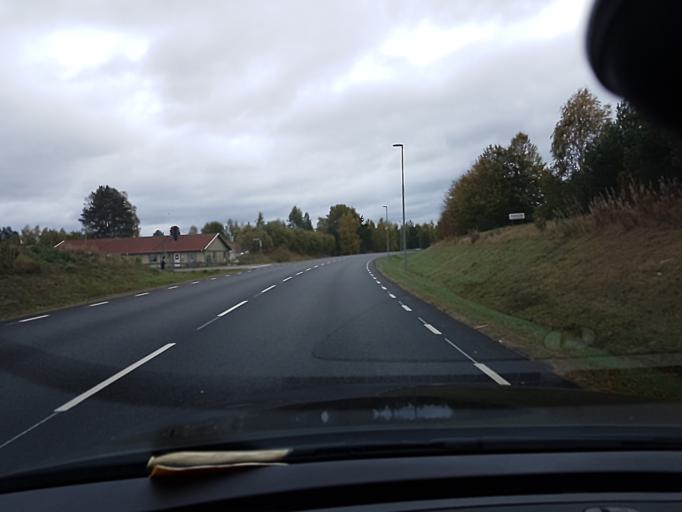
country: SE
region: Kronoberg
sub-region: Vaxjo Kommun
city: Vaexjoe
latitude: 56.9119
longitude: 14.7995
